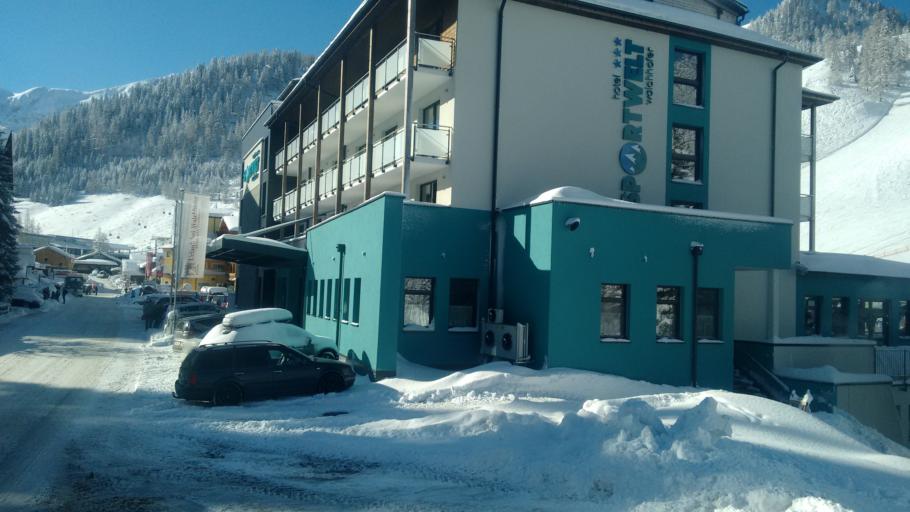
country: AT
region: Salzburg
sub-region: Politischer Bezirk Sankt Johann im Pongau
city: Untertauern
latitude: 47.2951
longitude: 13.4569
